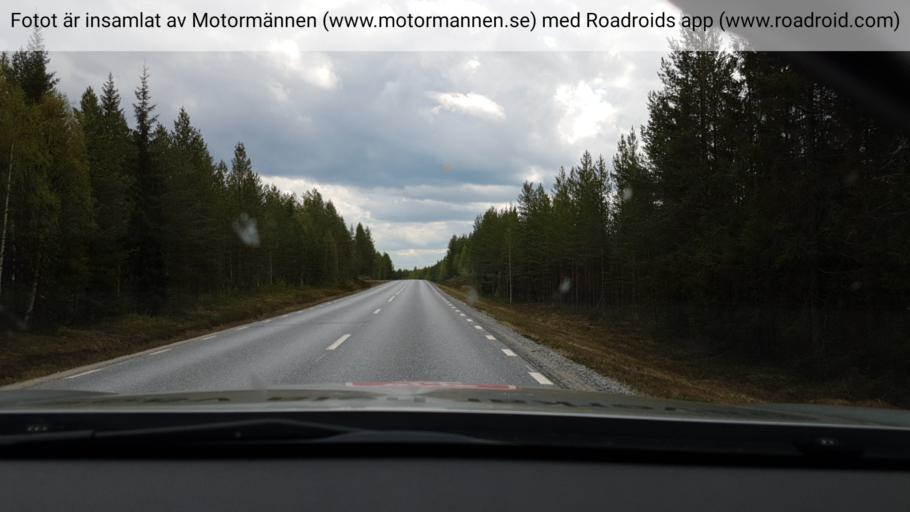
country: SE
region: Vaesterbotten
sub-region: Bjurholms Kommun
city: Bjurholm
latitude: 64.0207
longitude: 18.6737
